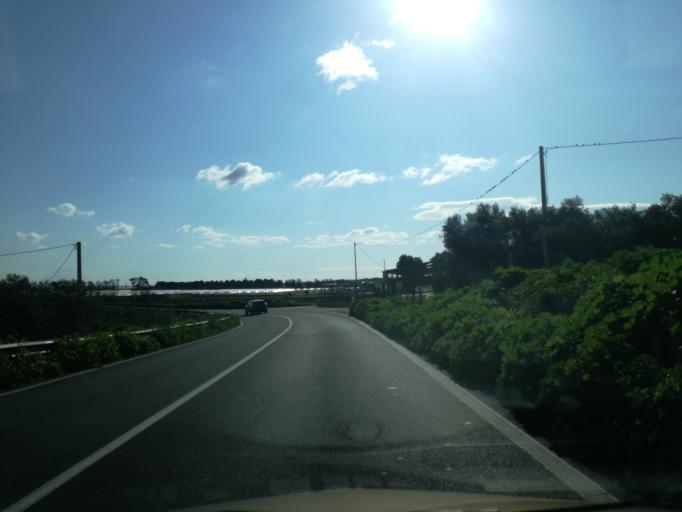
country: IT
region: Sicily
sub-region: Ragusa
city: Acate
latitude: 36.9830
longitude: 14.4528
